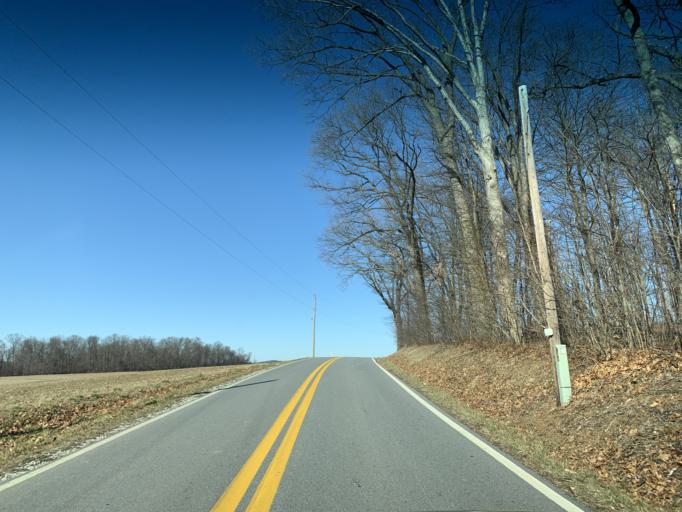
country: US
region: Maryland
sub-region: Carroll County
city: Westminster
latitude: 39.6364
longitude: -76.9692
